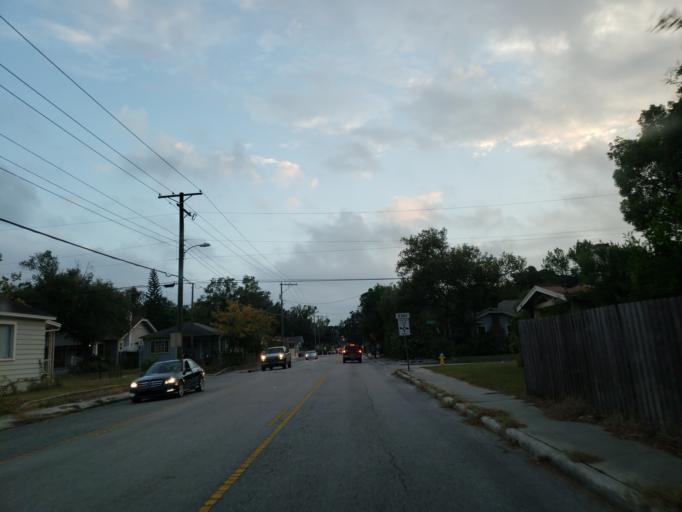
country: US
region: Florida
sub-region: Hillsborough County
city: Tampa
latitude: 27.9919
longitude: -82.4621
